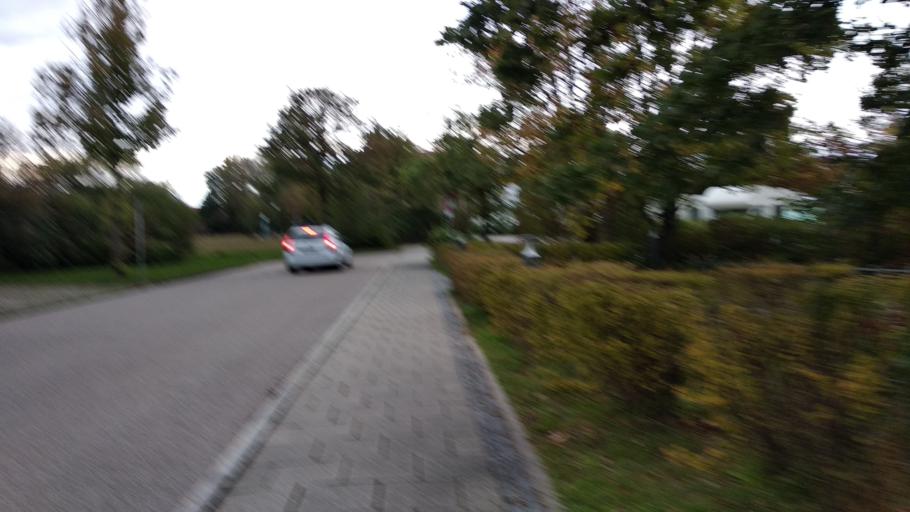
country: DE
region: Bavaria
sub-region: Upper Bavaria
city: Putzbrunn
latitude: 48.0736
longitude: 11.7213
